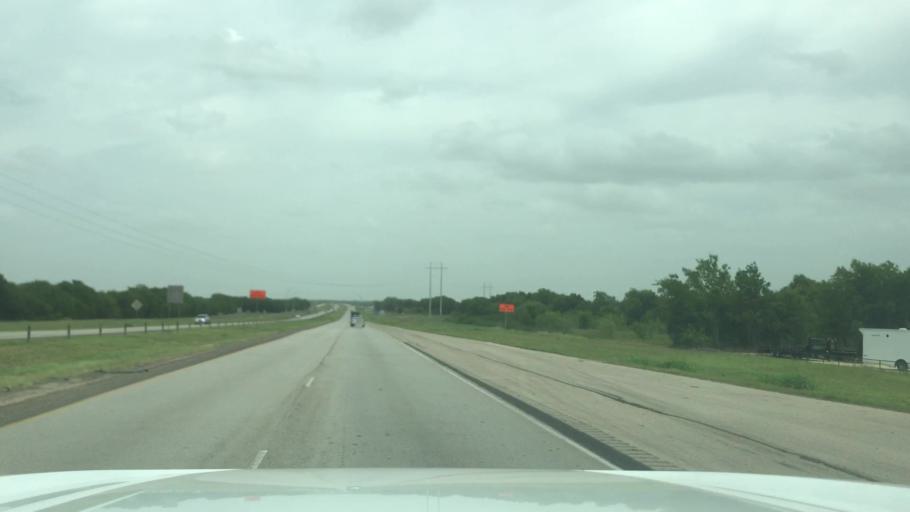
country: US
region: Texas
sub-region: McLennan County
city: Beverly
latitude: 31.5009
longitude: -97.1199
